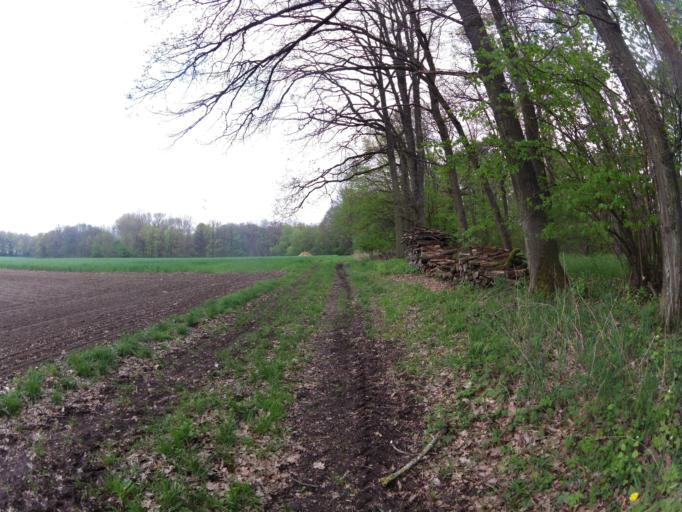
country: DE
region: Bavaria
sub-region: Regierungsbezirk Unterfranken
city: Ochsenfurt
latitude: 49.7012
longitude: 10.0634
